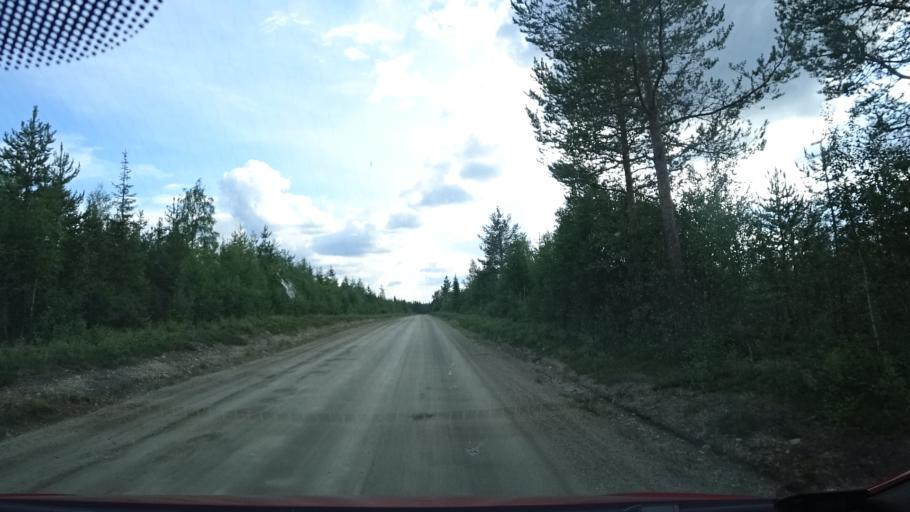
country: FI
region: Lapland
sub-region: Tunturi-Lappi
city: Kittilae
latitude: 68.0409
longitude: 25.2622
